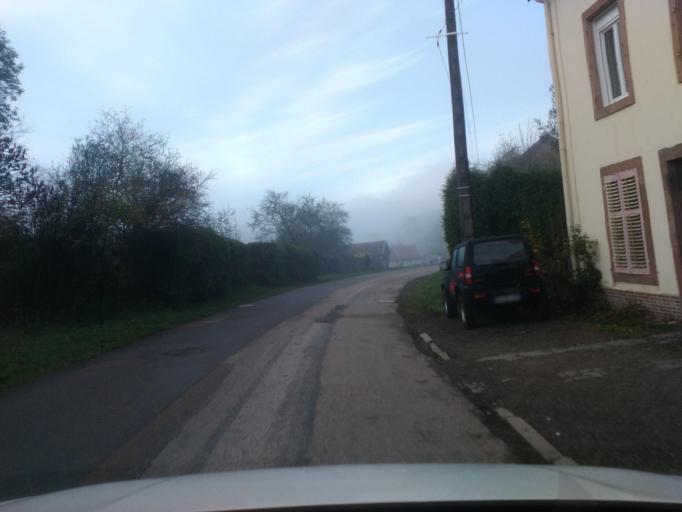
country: FR
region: Lorraine
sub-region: Departement des Vosges
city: Senones
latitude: 48.4245
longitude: 7.0158
